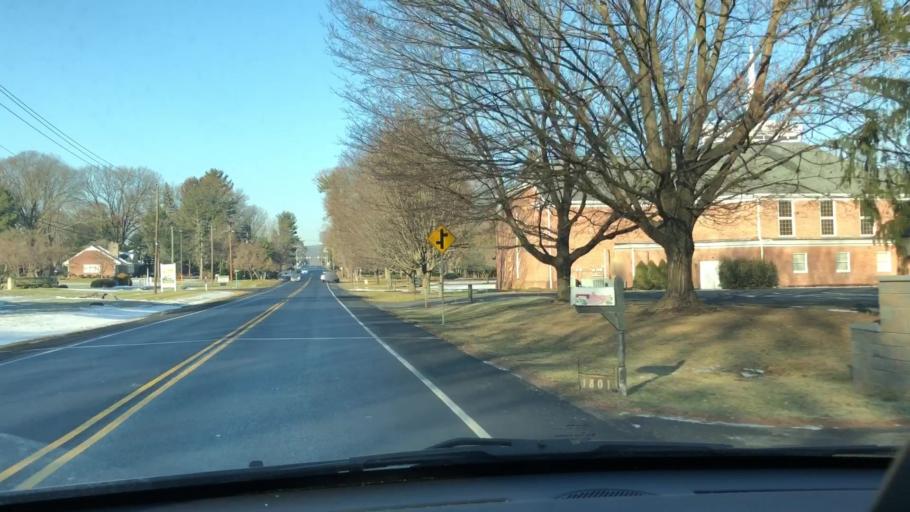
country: US
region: Pennsylvania
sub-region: Lancaster County
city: Lancaster
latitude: 40.0497
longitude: -76.3486
